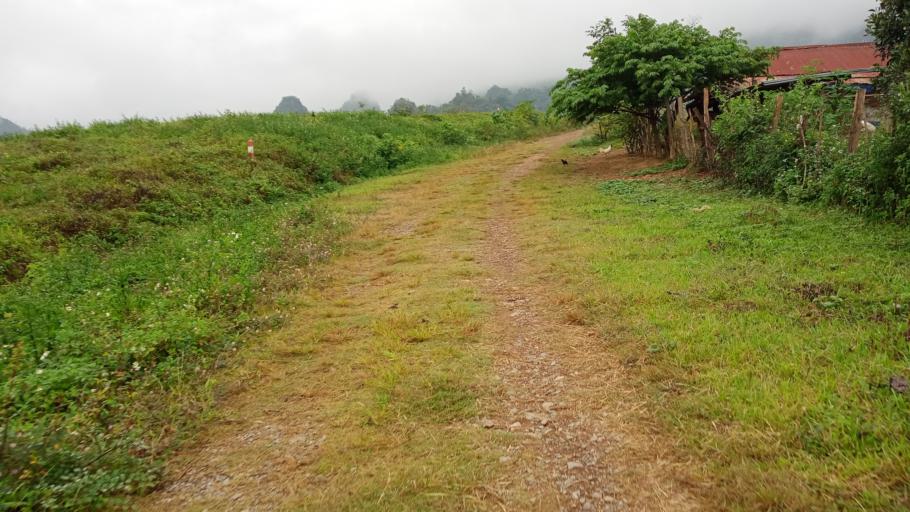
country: LA
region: Xiangkhoang
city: Phonsavan
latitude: 19.1037
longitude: 102.9277
